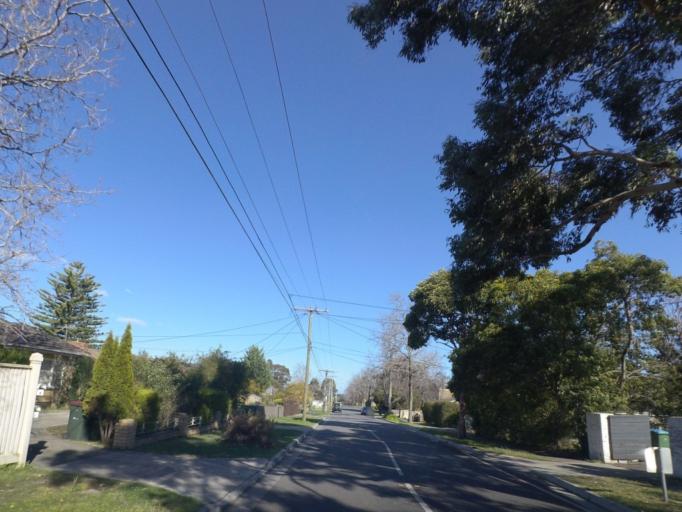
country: AU
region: Victoria
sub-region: Maroondah
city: Ringwood East
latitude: -37.8180
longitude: 145.2342
